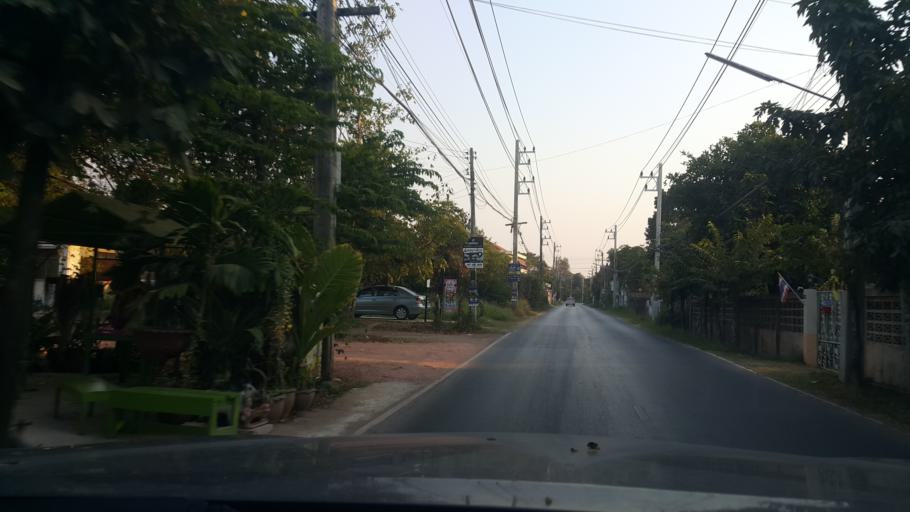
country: TH
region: Nakhon Ratchasima
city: Nakhon Ratchasima
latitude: 14.9461
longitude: 102.0284
